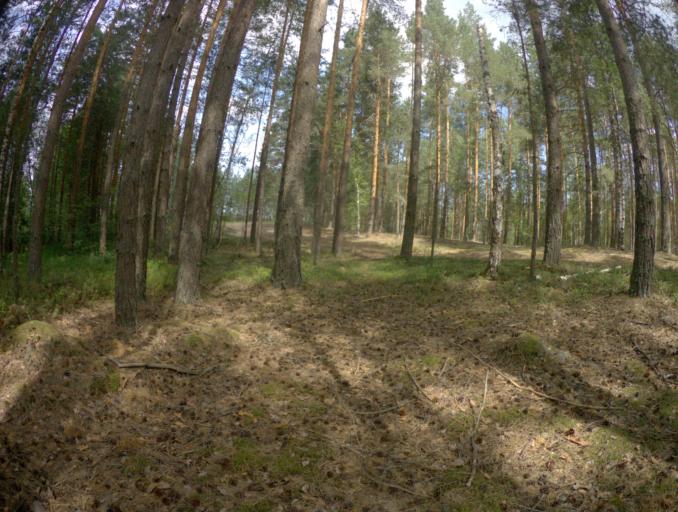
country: RU
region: Ivanovo
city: Talitsy
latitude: 56.3905
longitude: 42.3445
